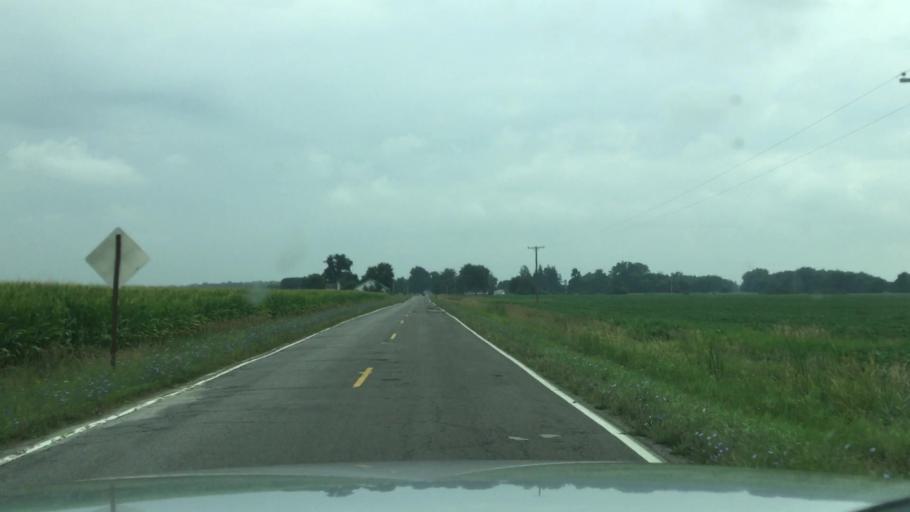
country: US
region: Michigan
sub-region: Shiawassee County
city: New Haven
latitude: 43.0991
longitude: -84.2259
